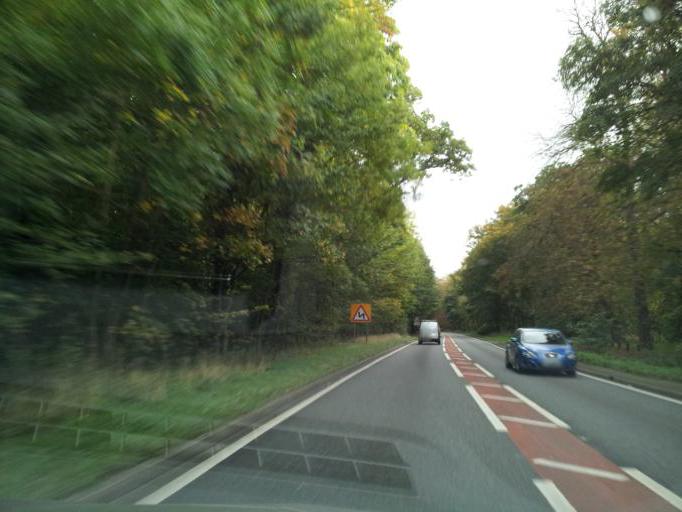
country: GB
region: England
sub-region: Cambridgeshire
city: Papworth Everard
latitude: 52.2237
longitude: -0.1659
